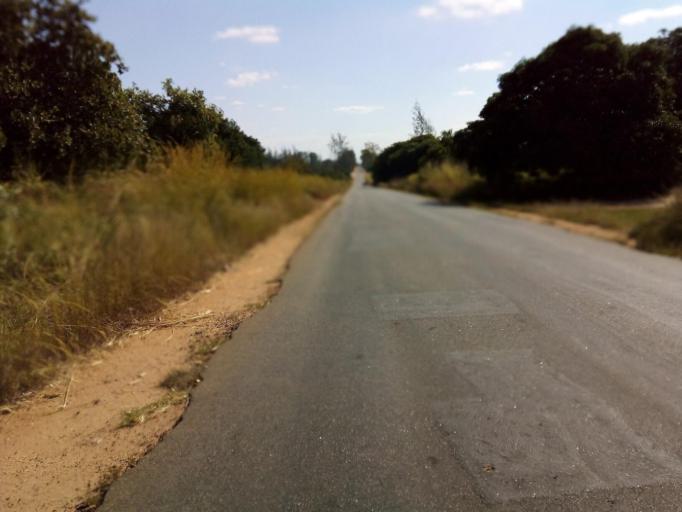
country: MZ
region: Zambezia
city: Quelimane
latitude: -17.5766
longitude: 36.6501
